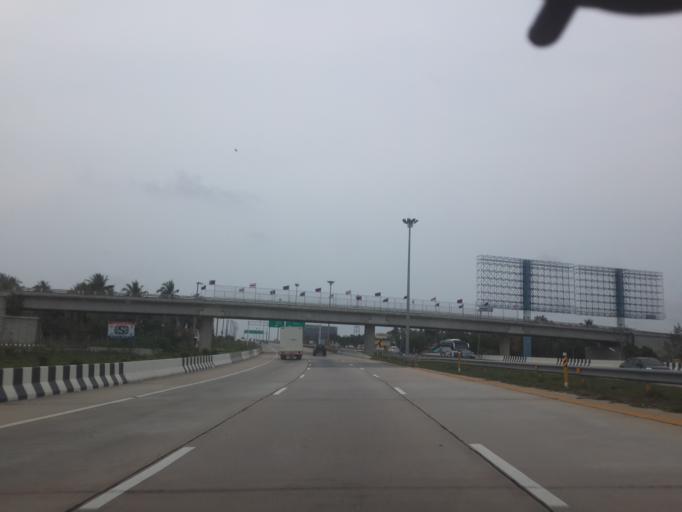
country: TH
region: Chon Buri
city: Phatthaya
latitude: 12.9543
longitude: 100.9722
